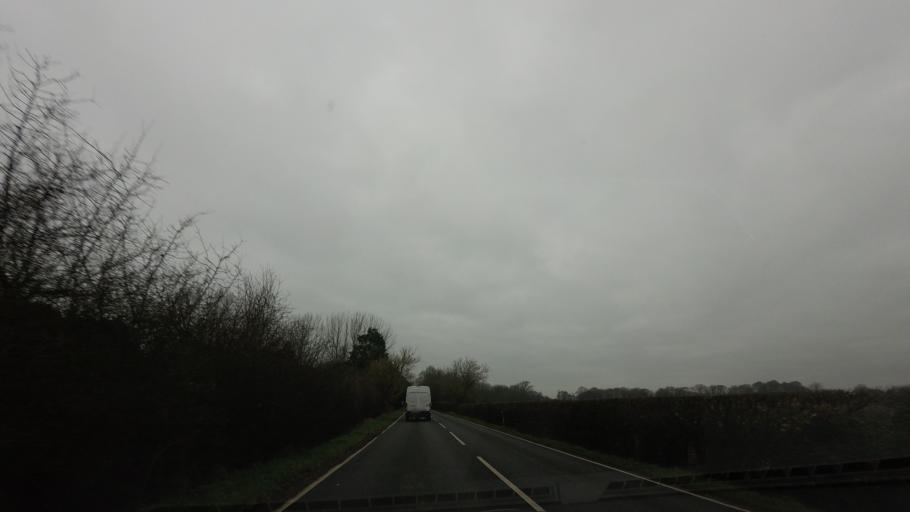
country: GB
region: England
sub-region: Kent
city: Staplehurst
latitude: 51.1429
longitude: 0.5522
